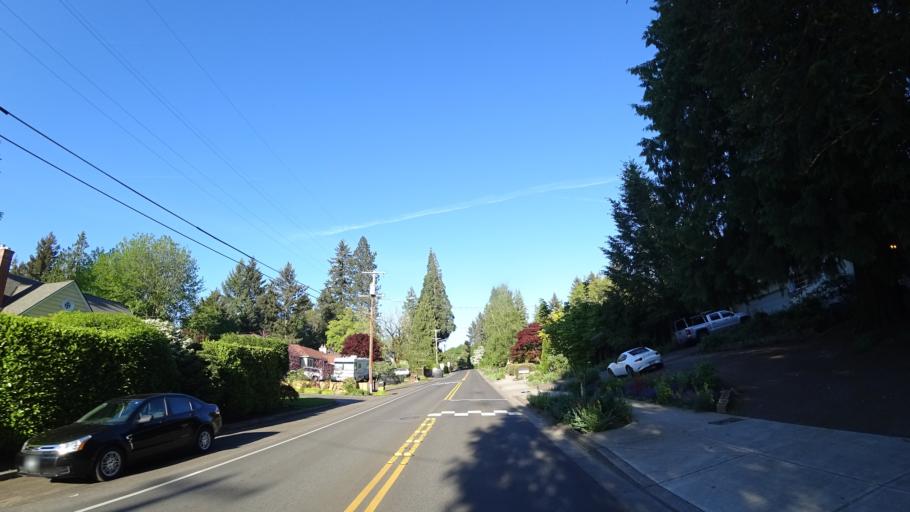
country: US
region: Oregon
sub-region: Washington County
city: West Slope
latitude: 45.4921
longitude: -122.7631
